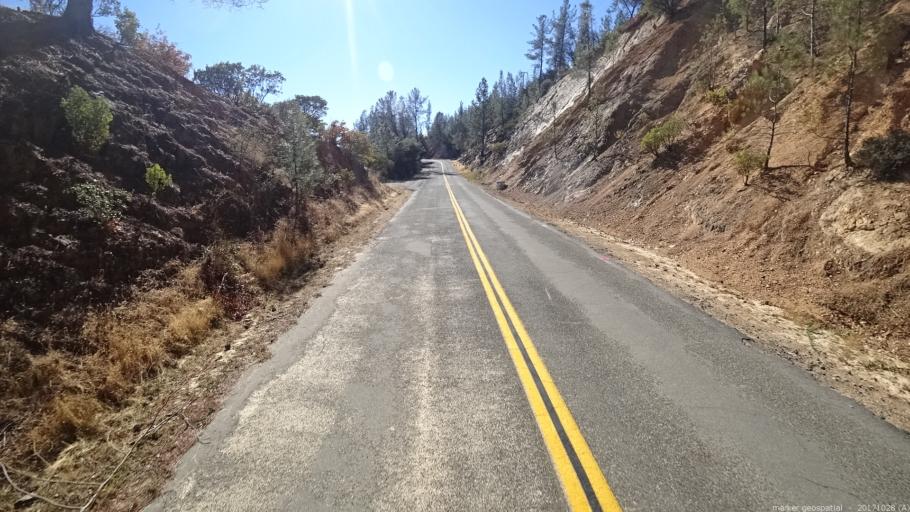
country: US
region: California
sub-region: Shasta County
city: Shasta
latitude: 40.6525
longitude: -122.5573
